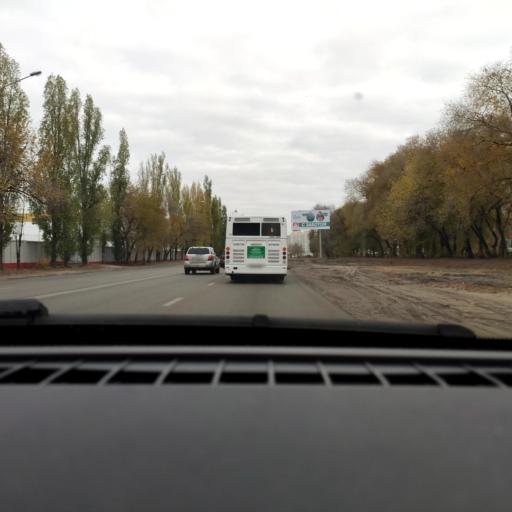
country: RU
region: Voronezj
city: Voronezh
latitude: 51.6388
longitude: 39.2647
